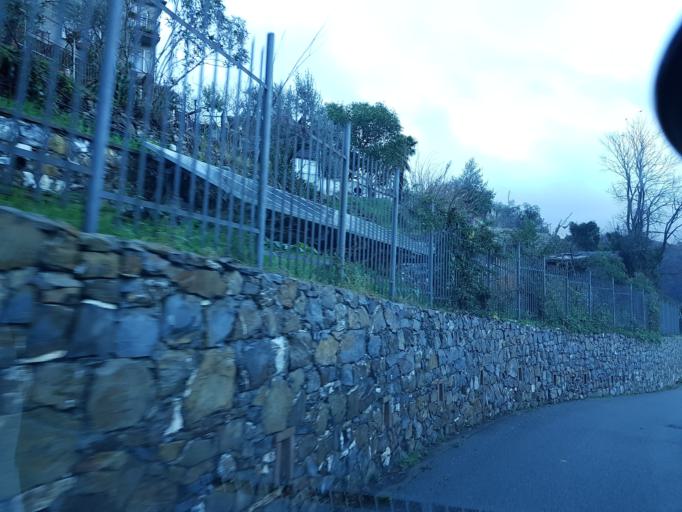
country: IT
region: Liguria
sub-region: Provincia di Genova
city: Genoa
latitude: 44.4340
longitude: 8.9526
